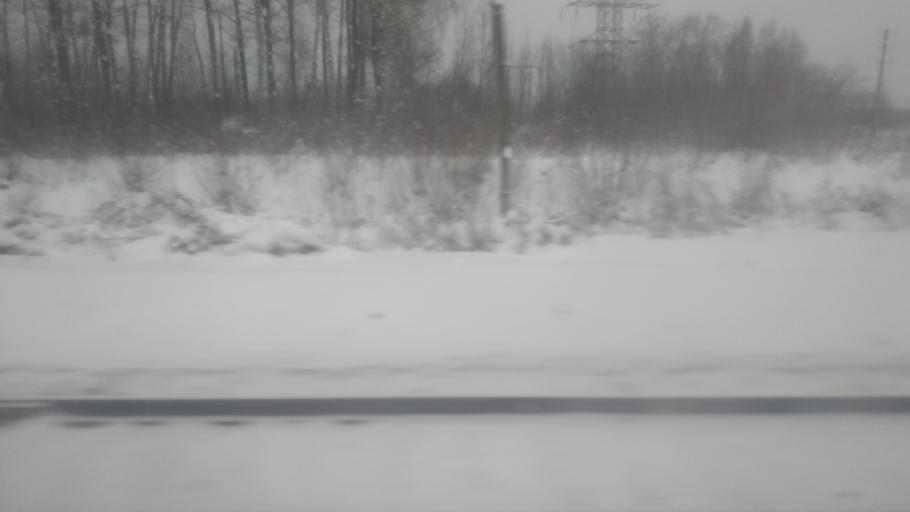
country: RU
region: Bashkortostan
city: Amzya
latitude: 56.2401
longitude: 54.5425
